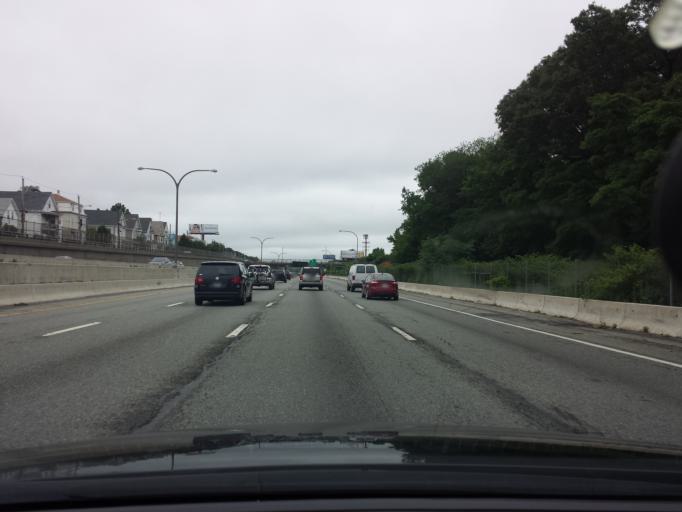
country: US
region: Rhode Island
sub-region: Providence County
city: Cranston
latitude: 41.7923
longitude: -71.4132
